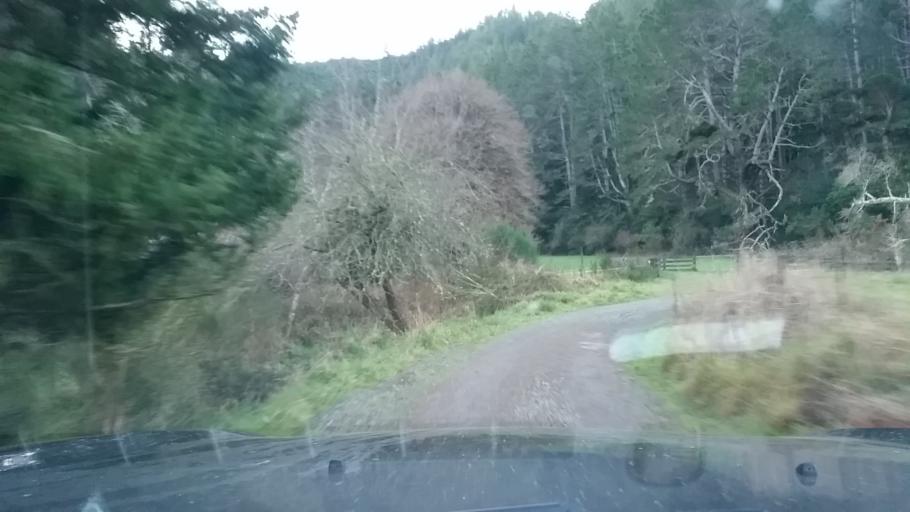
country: NZ
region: Marlborough
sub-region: Marlborough District
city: Blenheim
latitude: -41.4689
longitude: 173.7437
